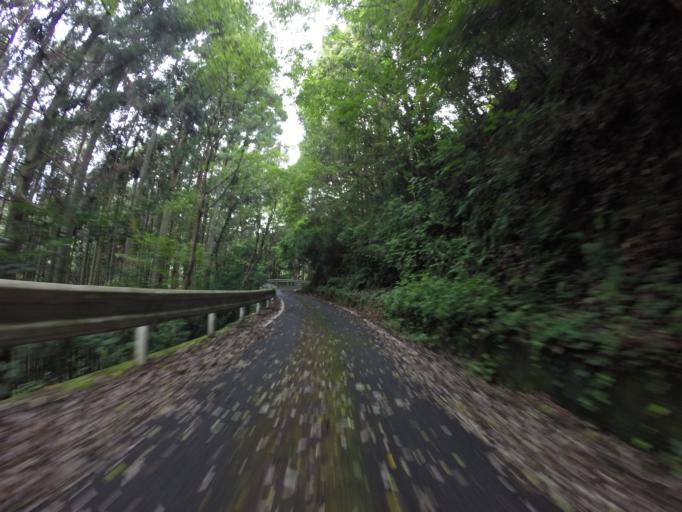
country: JP
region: Shizuoka
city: Shizuoka-shi
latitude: 35.0330
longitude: 138.3034
